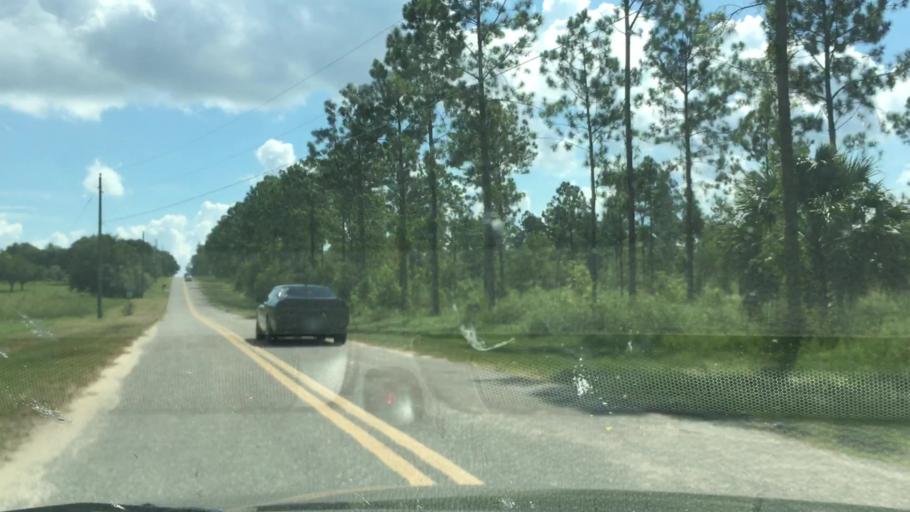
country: US
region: Florida
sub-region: Lake County
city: Minneola
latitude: 28.6376
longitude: -81.7309
